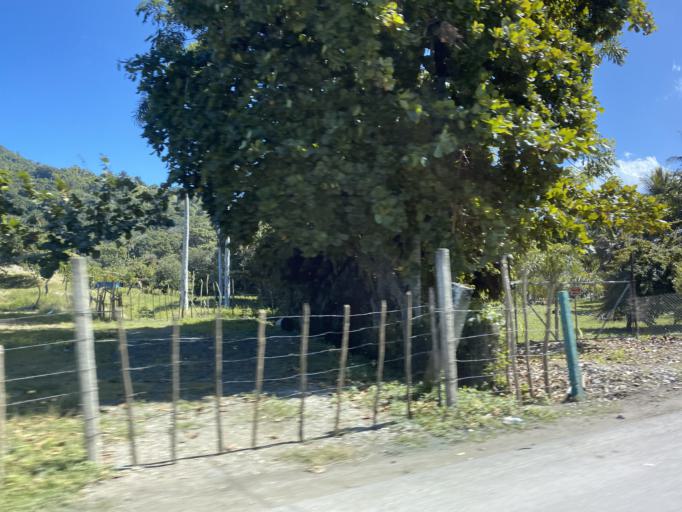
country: DO
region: Puerto Plata
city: Imbert
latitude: 19.8117
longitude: -70.7791
